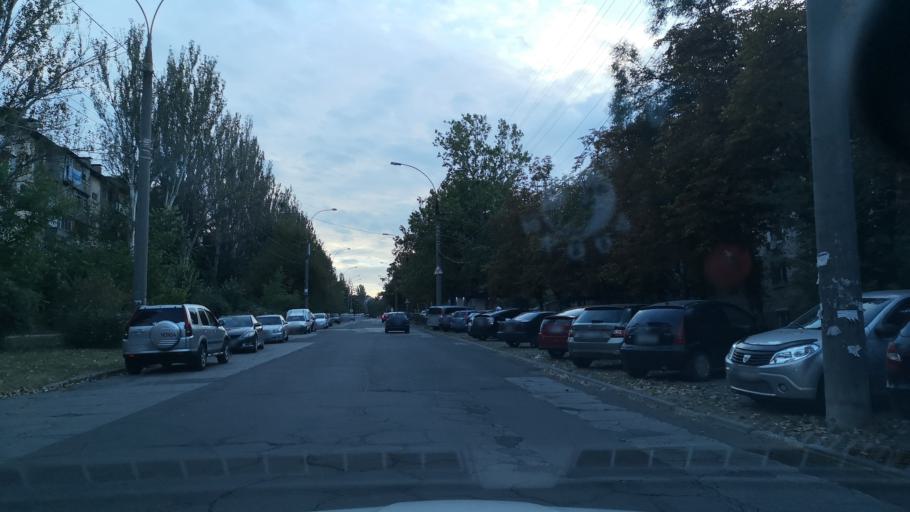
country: MD
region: Chisinau
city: Chisinau
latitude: 46.9880
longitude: 28.8521
